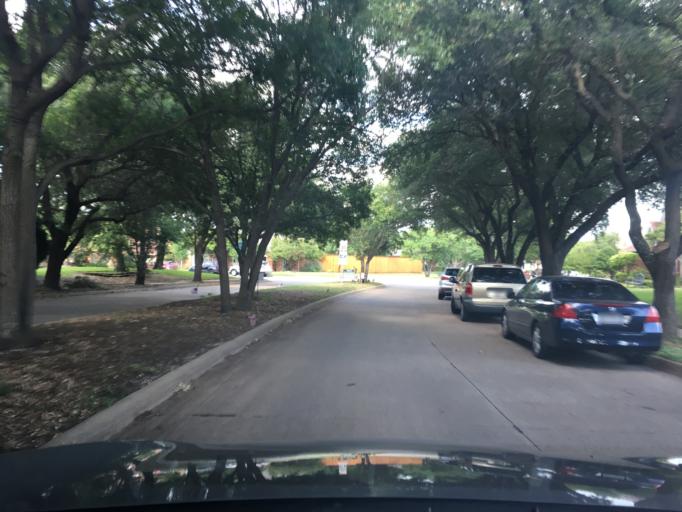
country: US
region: Texas
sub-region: Dallas County
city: Richardson
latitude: 32.9413
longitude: -96.6823
